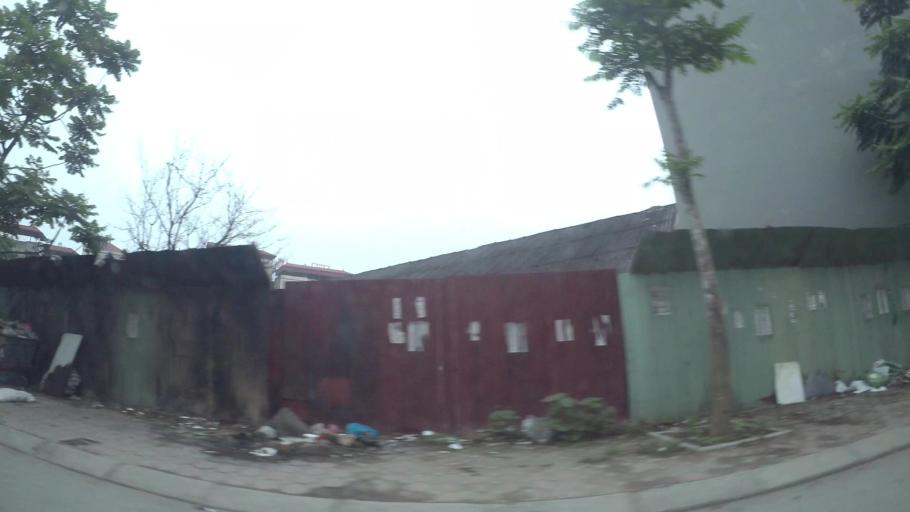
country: VN
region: Ha Noi
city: Hai BaTrung
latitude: 20.9866
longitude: 105.8356
